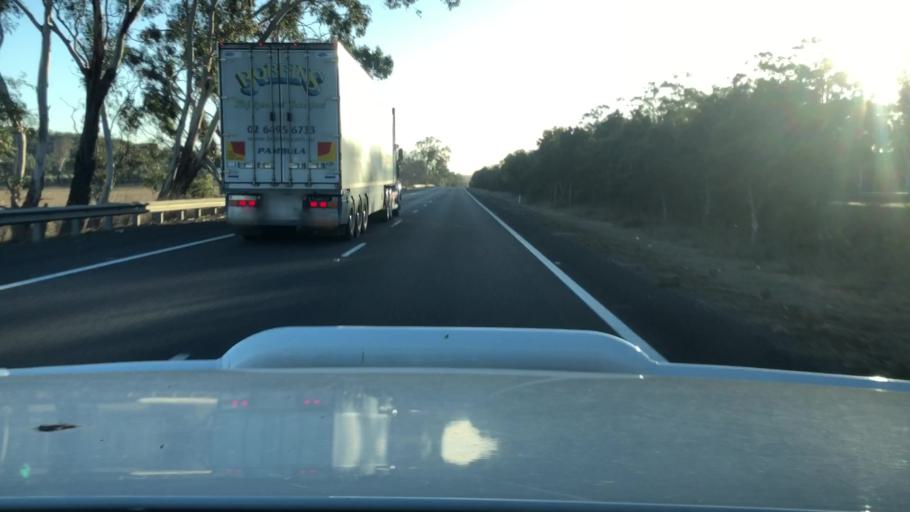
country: AU
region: New South Wales
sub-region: Wingecarribee
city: Bundanoon
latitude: -34.6697
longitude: 150.0674
